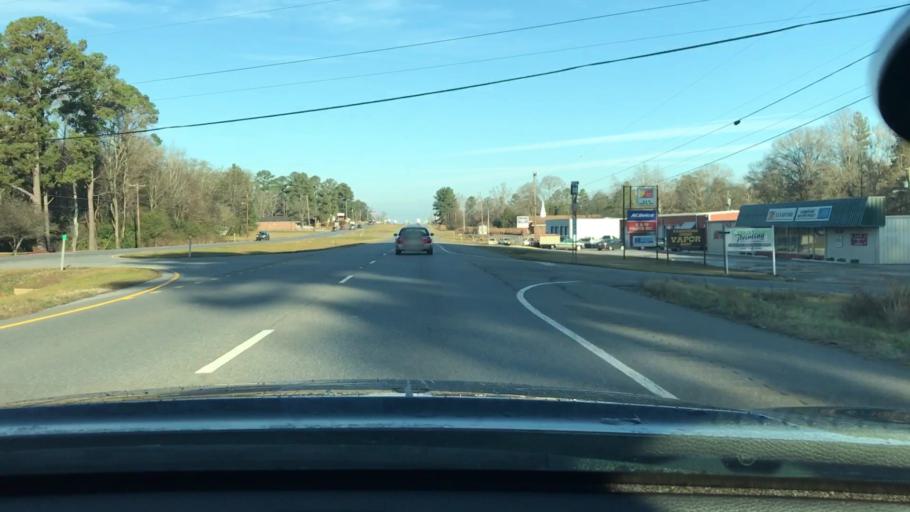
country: US
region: Alabama
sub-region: Talladega County
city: Childersburg
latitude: 33.2511
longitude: -86.3409
